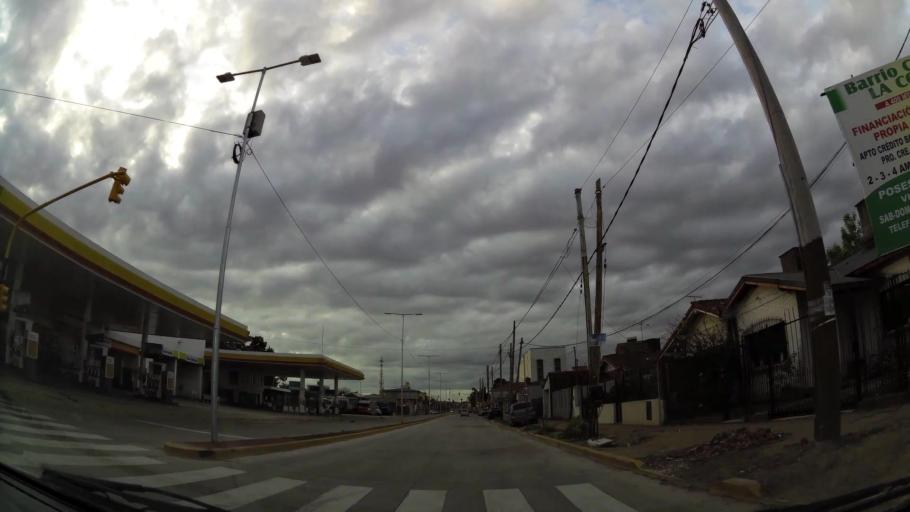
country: AR
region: Buenos Aires
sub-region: Partido de Quilmes
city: Quilmes
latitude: -34.7473
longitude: -58.2254
